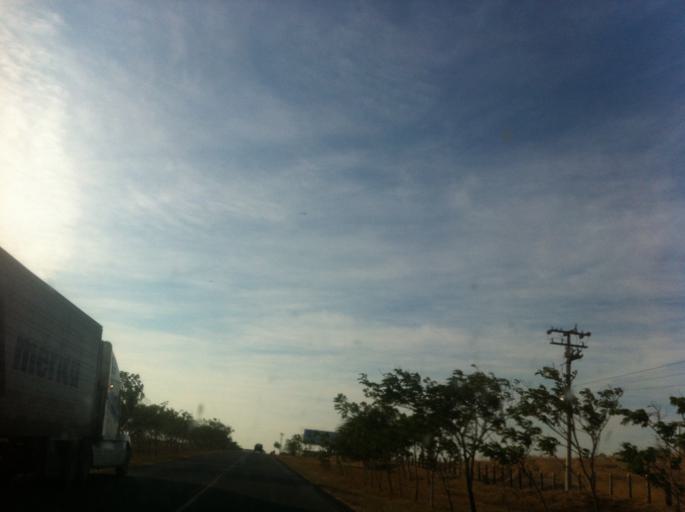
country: NI
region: Rivas
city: Rivas
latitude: 11.3437
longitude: -85.7354
